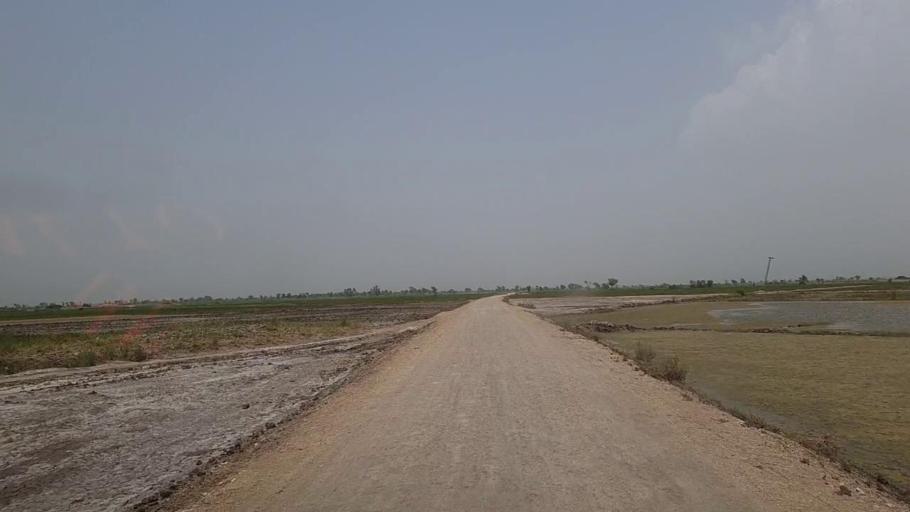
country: PK
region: Sindh
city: Sita Road
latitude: 27.0714
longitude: 67.8659
